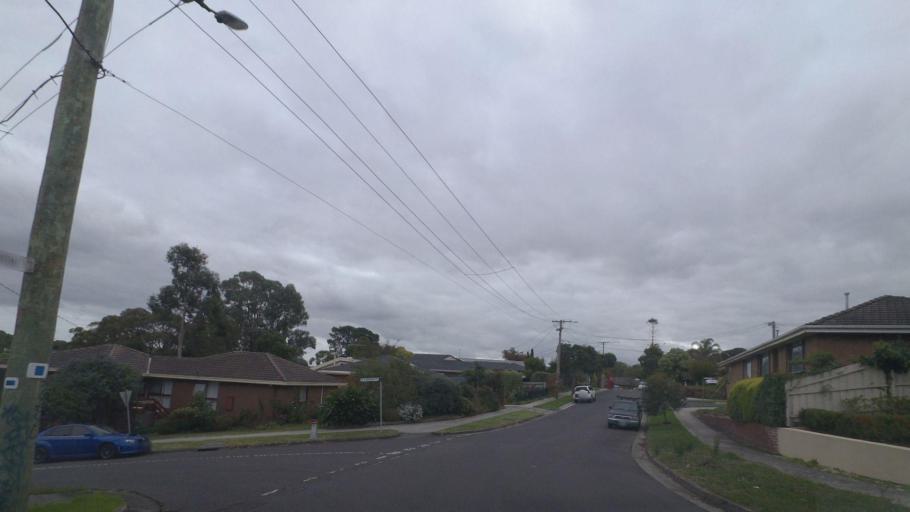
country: AU
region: Victoria
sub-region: Whitehorse
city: Nunawading
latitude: -37.8097
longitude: 145.1813
